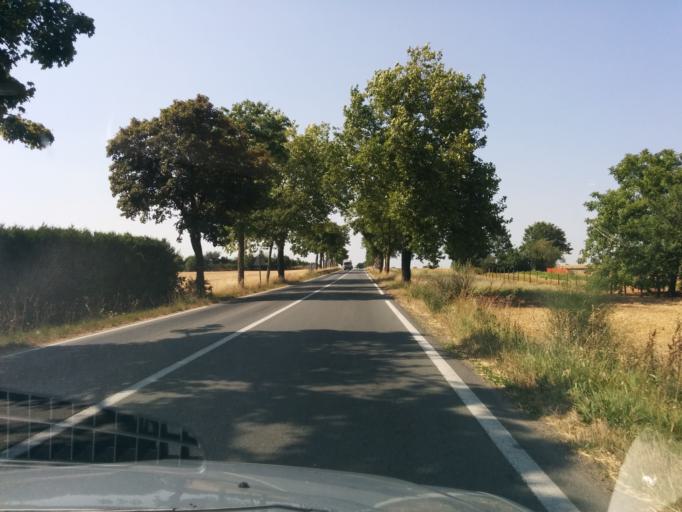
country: FR
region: Poitou-Charentes
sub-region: Departement de la Vienne
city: Neuville-de-Poitou
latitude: 46.6865
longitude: 0.2617
